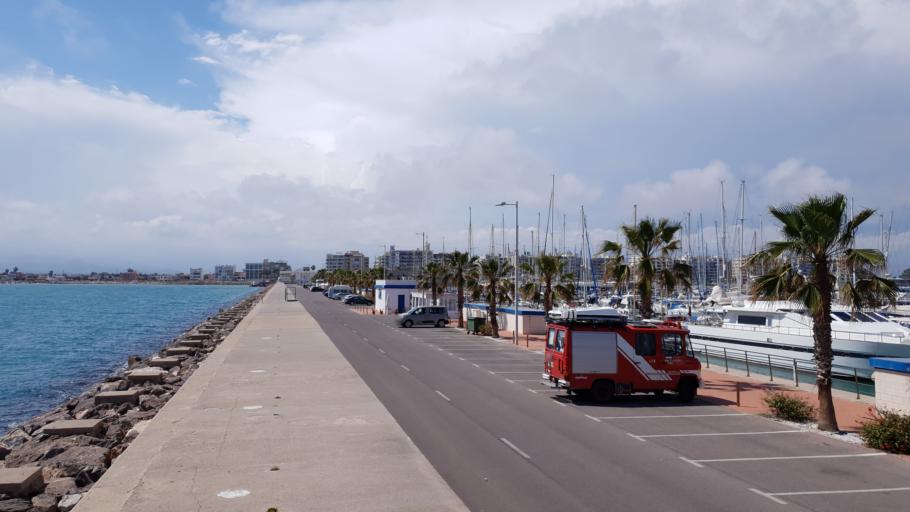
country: ES
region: Valencia
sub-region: Provincia de Castello
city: Burriana
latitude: 39.8588
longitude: -0.0708
